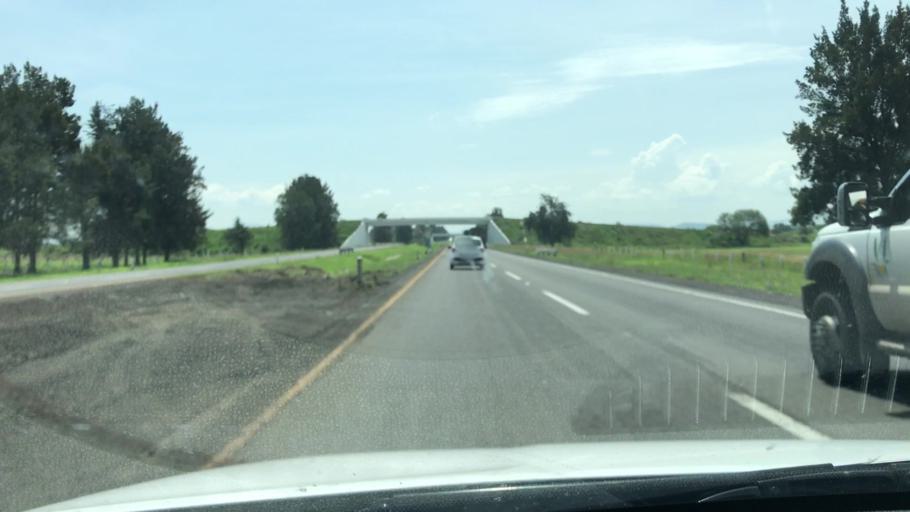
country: MX
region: Jalisco
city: La Barca
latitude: 20.3220
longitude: -102.5294
